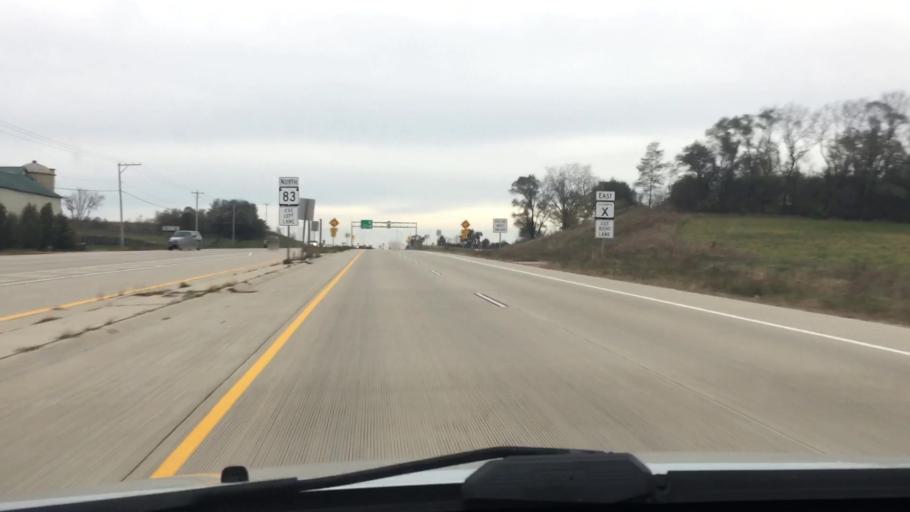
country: US
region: Wisconsin
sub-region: Waukesha County
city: North Prairie
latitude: 42.9311
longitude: -88.3463
